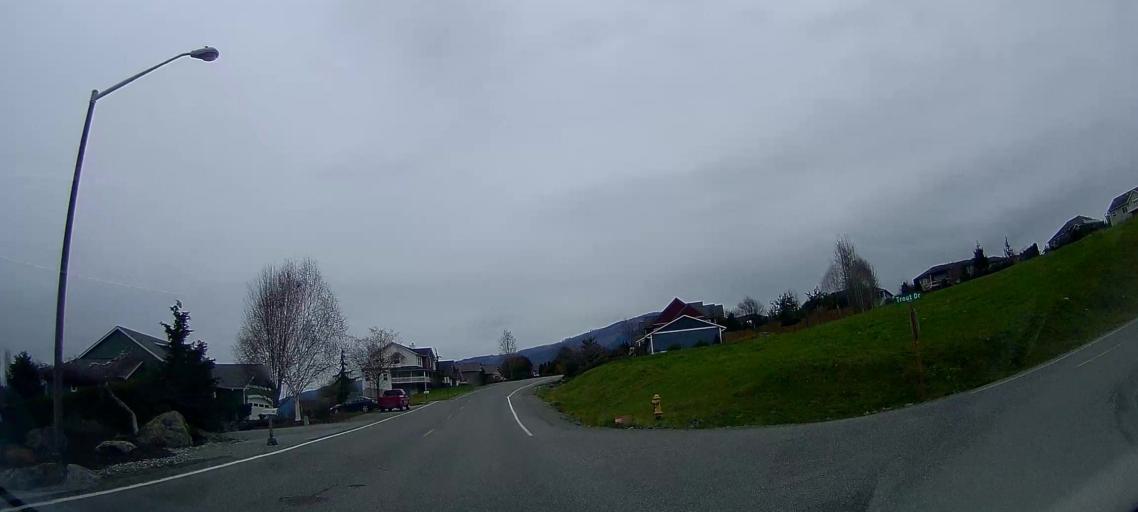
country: US
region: Washington
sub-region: Skagit County
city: Big Lake
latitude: 48.3996
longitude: -122.2335
